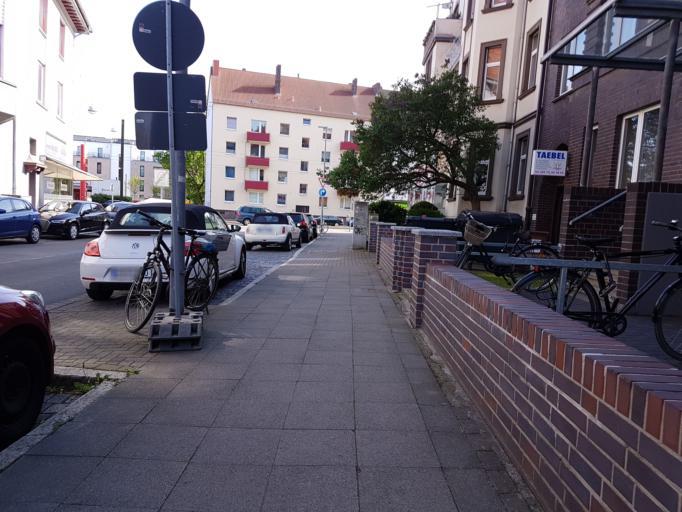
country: DE
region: Lower Saxony
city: Hannover
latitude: 52.3992
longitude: 9.7754
